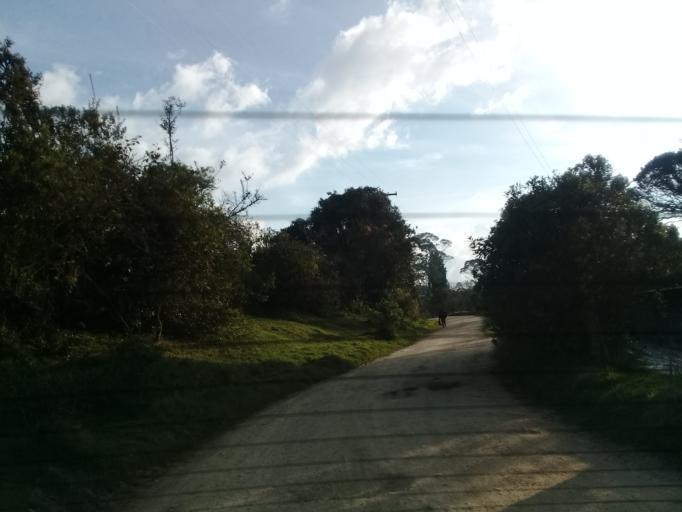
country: CO
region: Cundinamarca
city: Sibate
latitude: 4.4477
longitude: -74.2768
